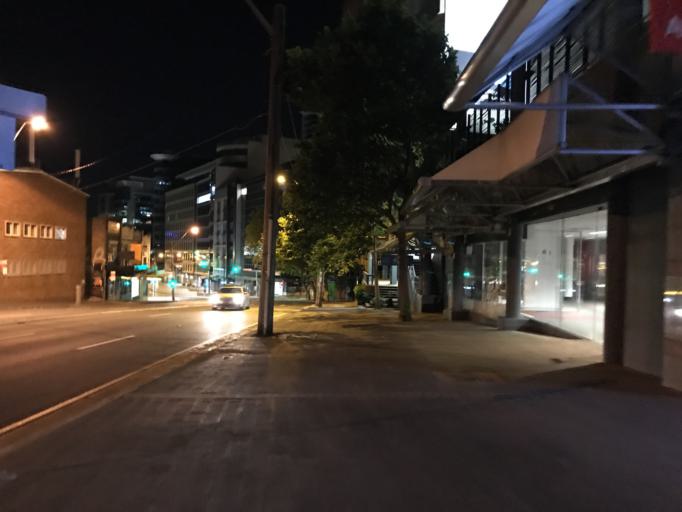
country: AU
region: New South Wales
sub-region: North Sydney
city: St Leonards
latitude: -33.8233
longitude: 151.1965
